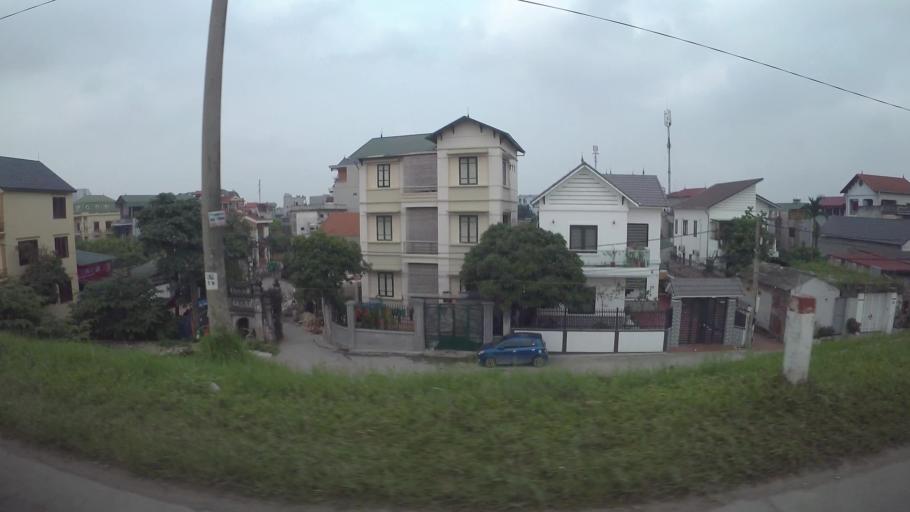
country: VN
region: Ha Noi
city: Trau Quy
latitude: 21.0083
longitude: 105.9067
